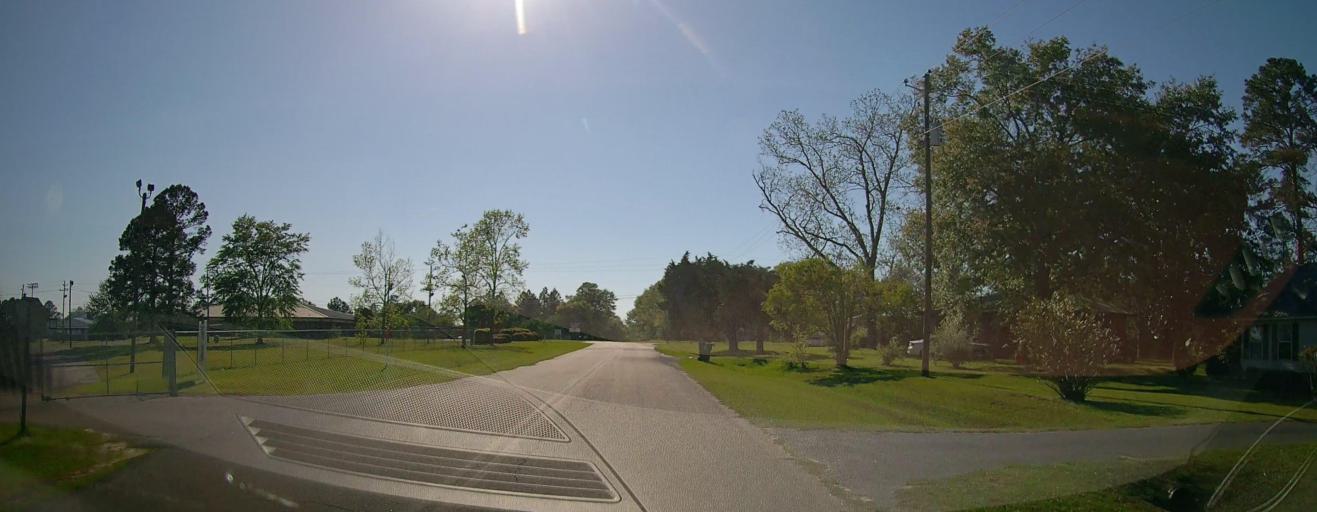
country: US
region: Georgia
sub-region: Wilcox County
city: Rochelle
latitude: 31.9440
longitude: -83.4519
